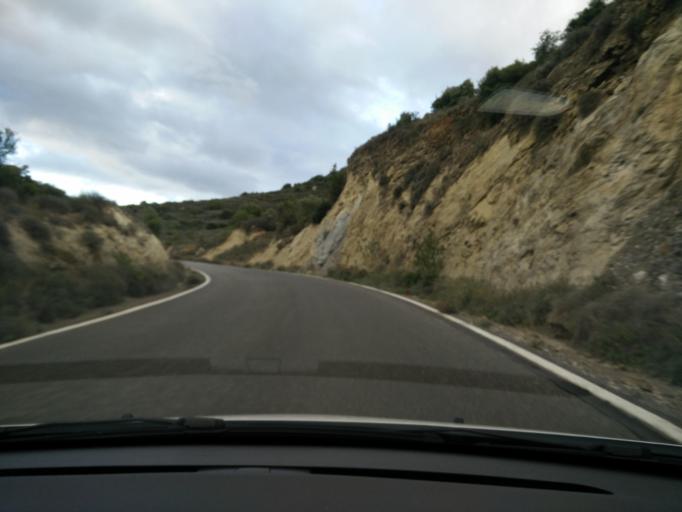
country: GR
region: Crete
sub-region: Nomos Lasithiou
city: Gra Liyia
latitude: 35.0907
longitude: 25.6922
